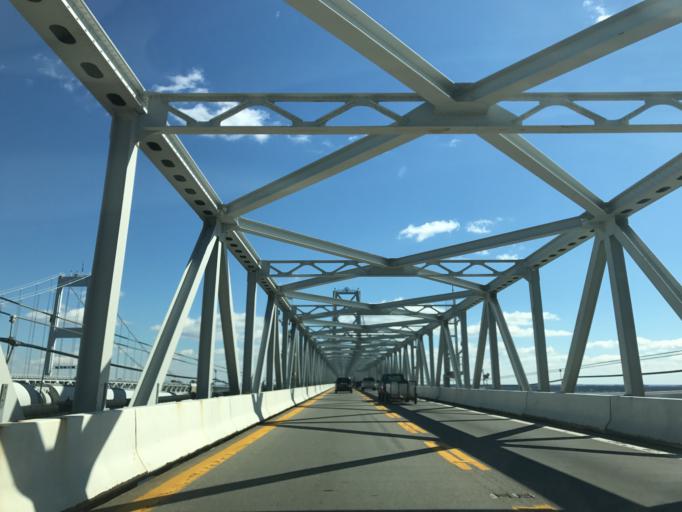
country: US
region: Maryland
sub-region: Queen Anne's County
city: Stevensville
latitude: 38.9946
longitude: -76.3806
